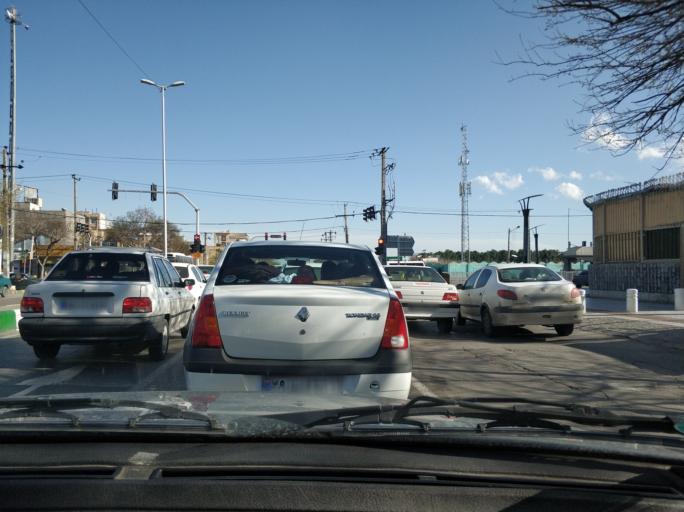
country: IR
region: Razavi Khorasan
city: Mashhad
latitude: 36.2995
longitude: 59.6332
